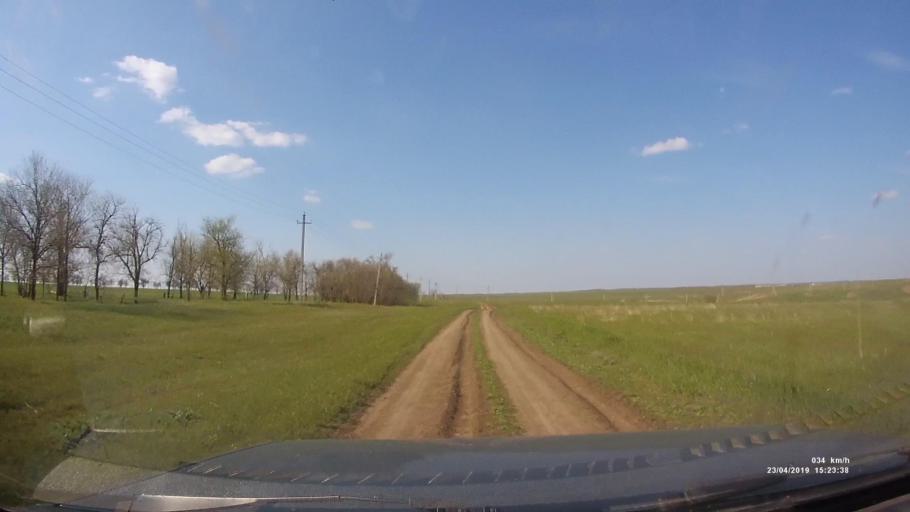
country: RU
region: Rostov
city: Remontnoye
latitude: 46.5368
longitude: 42.9697
